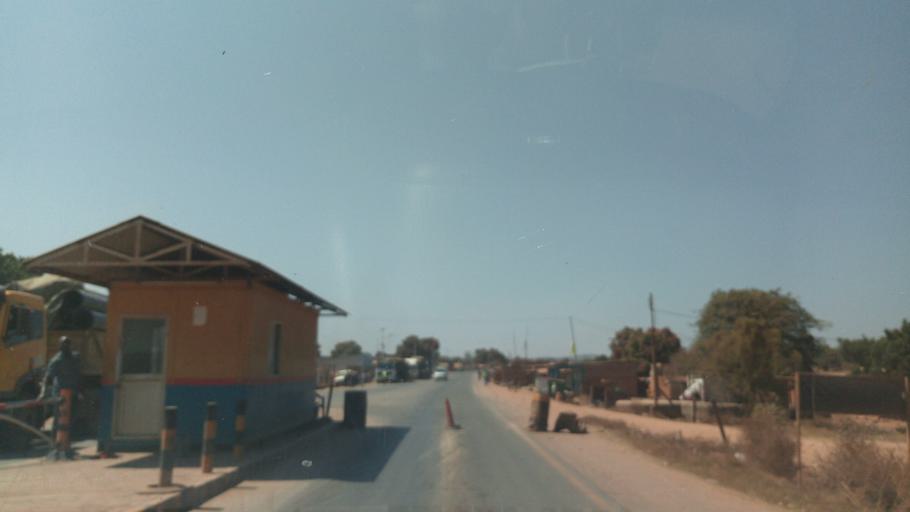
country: CD
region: Katanga
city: Kolwezi
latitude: -10.7806
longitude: 25.7304
